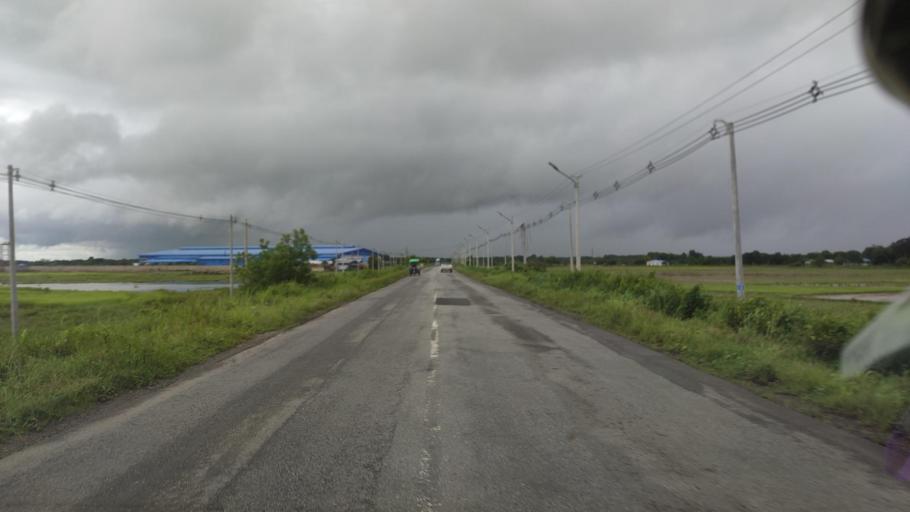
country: MM
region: Bago
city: Bago
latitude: 17.3736
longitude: 96.4711
